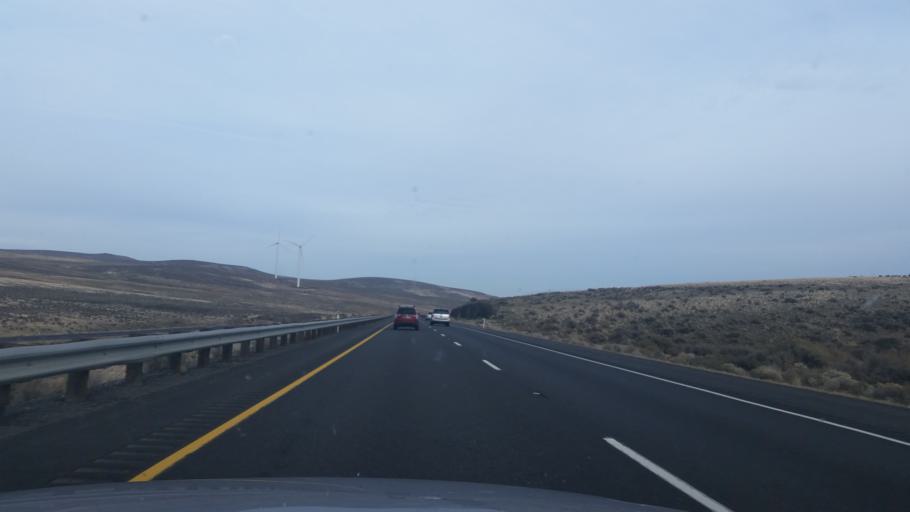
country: US
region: Washington
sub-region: Grant County
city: Mattawa
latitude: 46.9422
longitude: -120.1143
